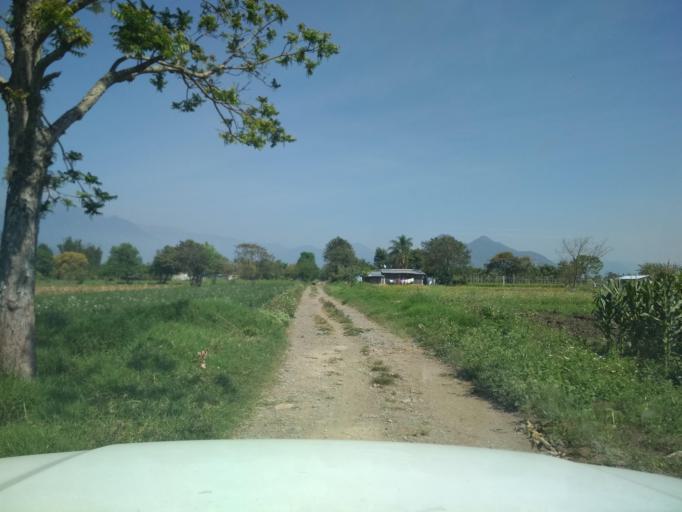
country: MX
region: Veracruz
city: Jalapilla
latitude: 18.8130
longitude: -97.0843
